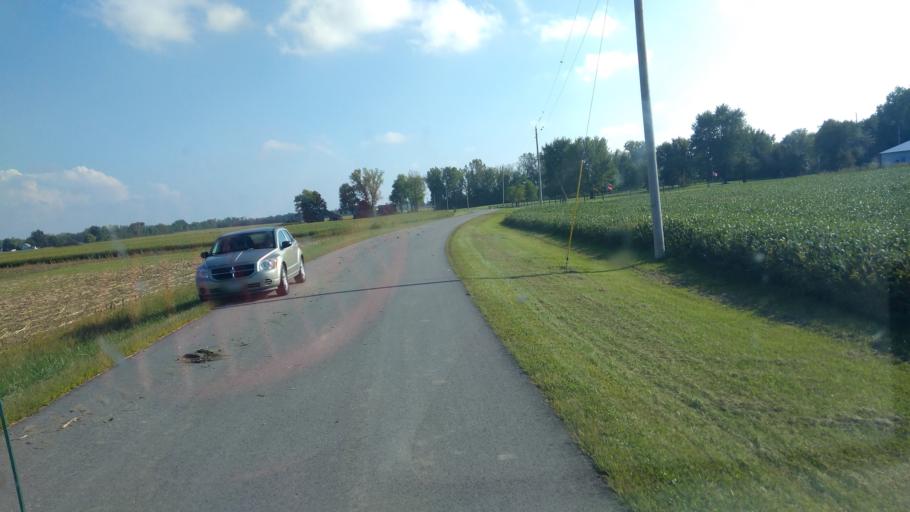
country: US
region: Ohio
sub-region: Hardin County
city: Forest
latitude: 40.7312
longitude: -83.4776
